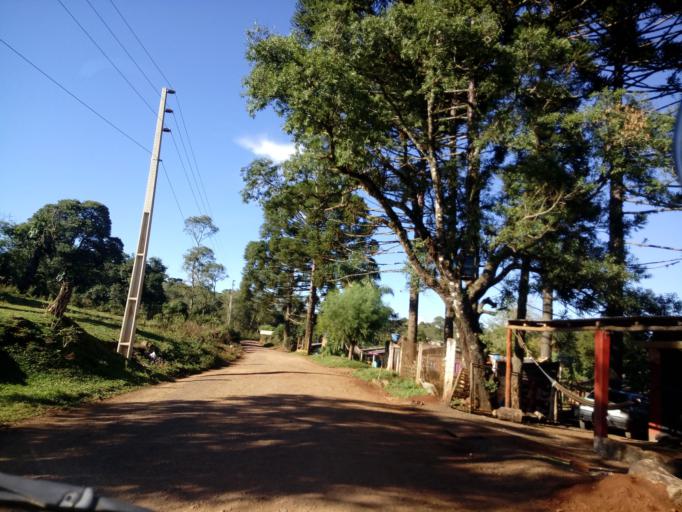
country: BR
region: Santa Catarina
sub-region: Chapeco
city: Chapeco
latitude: -27.2008
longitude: -52.6764
